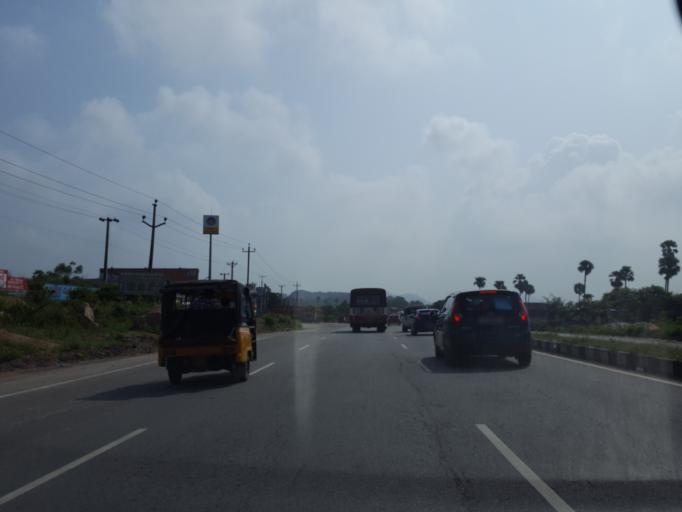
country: IN
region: Telangana
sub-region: Rangareddi
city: Ghatkesar
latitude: 17.3066
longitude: 78.7225
